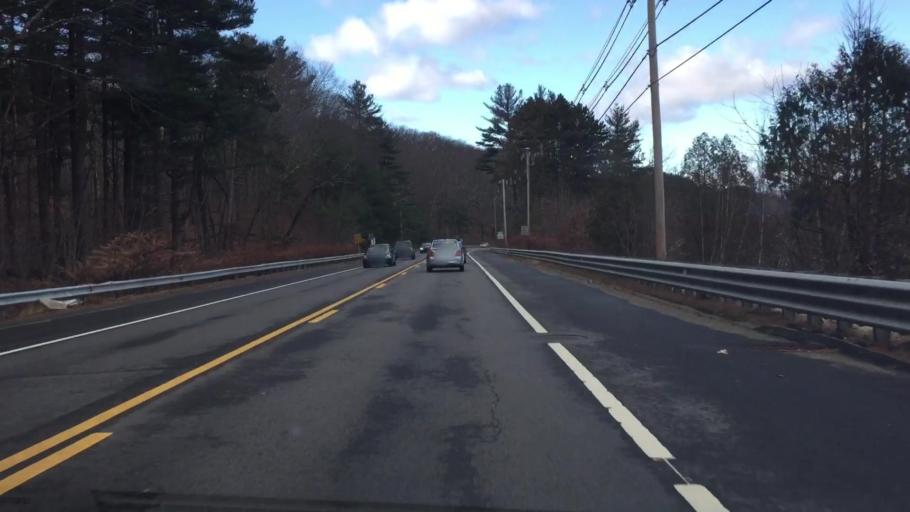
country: US
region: Massachusetts
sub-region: Worcester County
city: West Boylston
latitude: 42.3437
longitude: -71.7604
